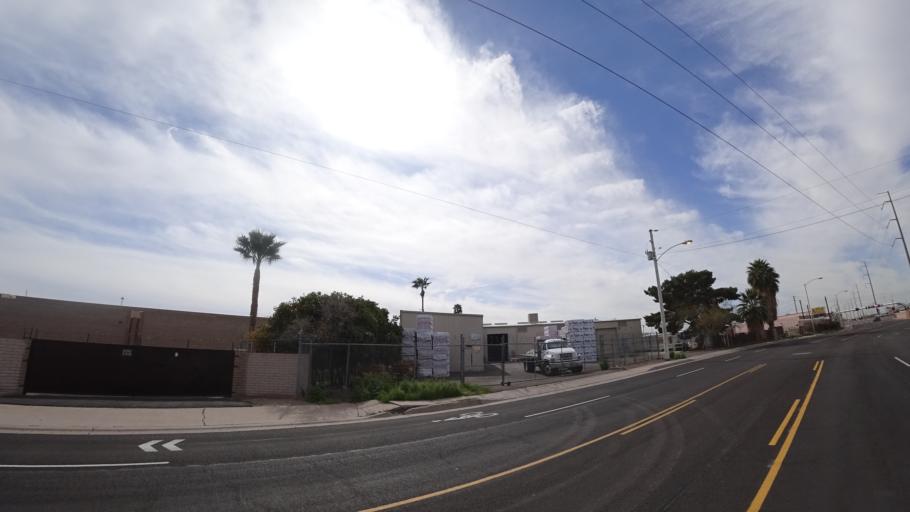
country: US
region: Arizona
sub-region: Maricopa County
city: Phoenix
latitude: 33.4732
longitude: -112.1061
